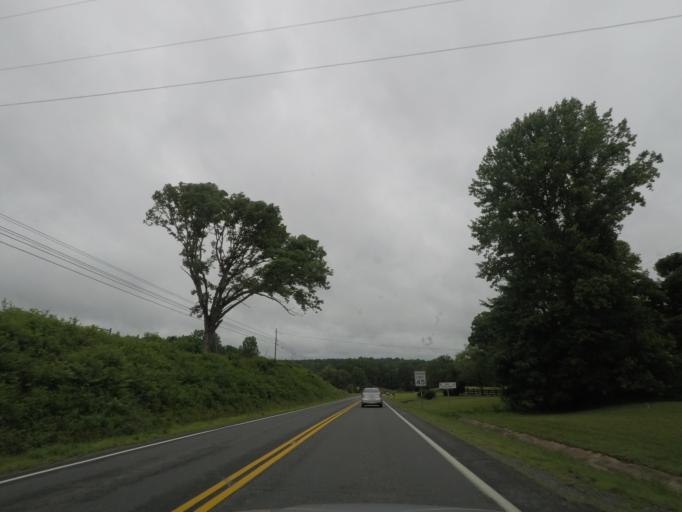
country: US
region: Virginia
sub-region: Fluvanna County
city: Palmyra
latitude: 37.8494
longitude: -78.2718
